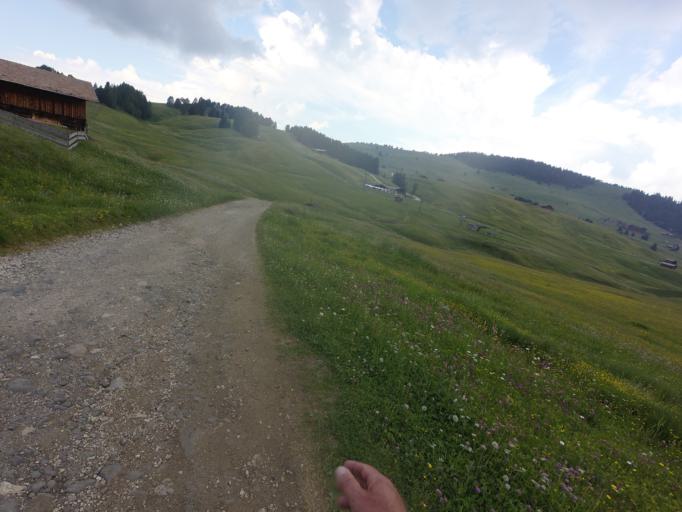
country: IT
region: Trentino-Alto Adige
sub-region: Bolzano
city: Ortisei
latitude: 46.5456
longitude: 11.6569
